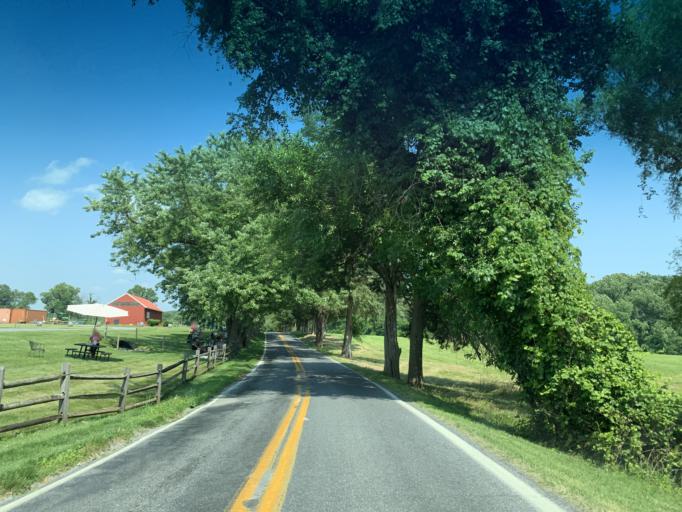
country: US
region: Maryland
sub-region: Frederick County
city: Urbana
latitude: 39.2505
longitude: -77.3792
